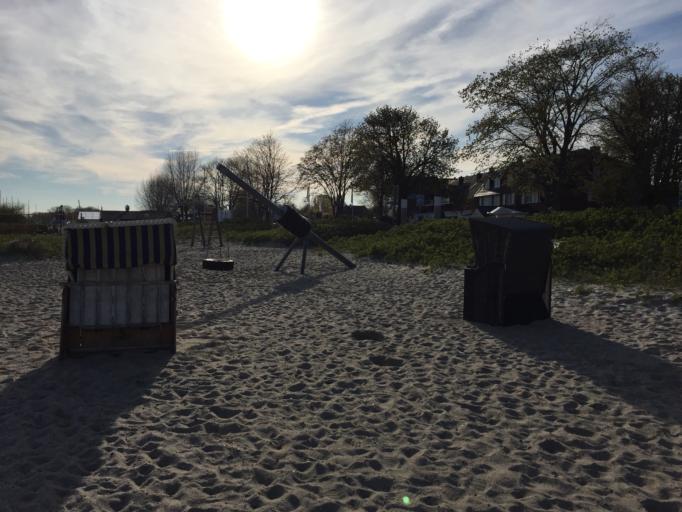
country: DE
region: Schleswig-Holstein
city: Strande
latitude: 54.4372
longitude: 10.1751
